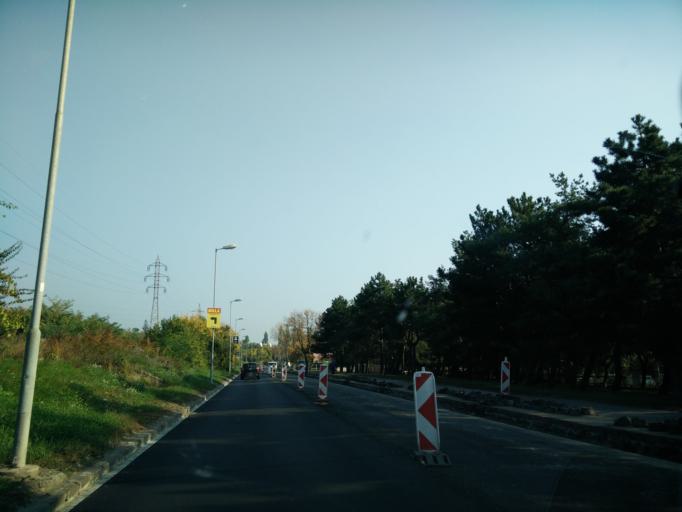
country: SK
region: Bratislavsky
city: Bratislava
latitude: 48.1659
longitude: 17.1212
